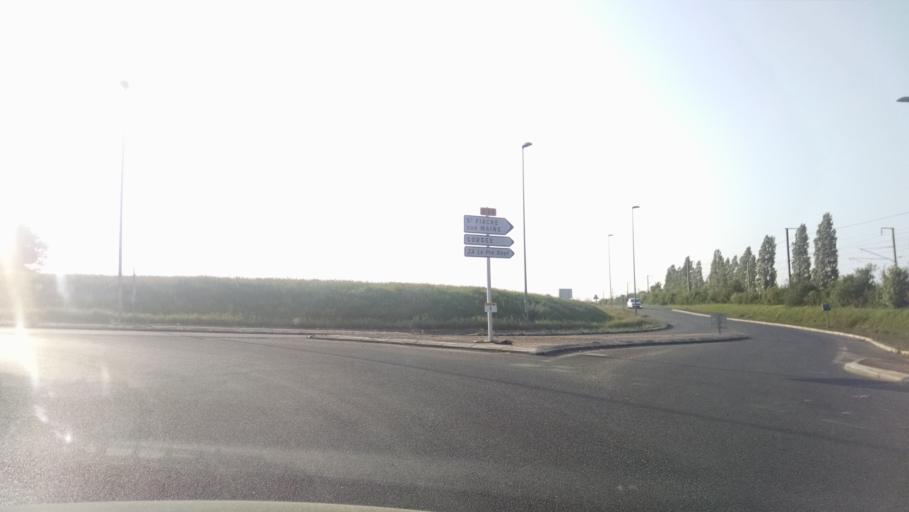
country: FR
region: Pays de la Loire
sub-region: Departement de la Loire-Atlantique
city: Gorges
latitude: 47.0948
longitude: -1.2992
